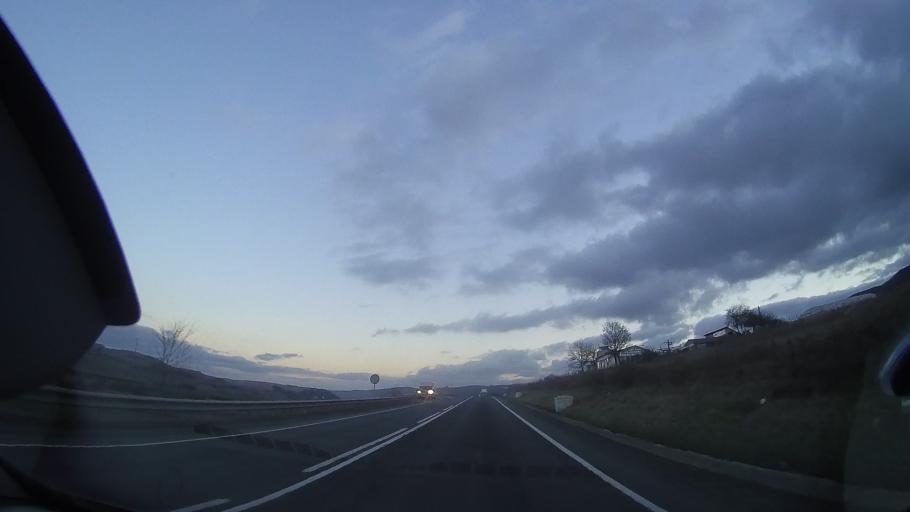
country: RO
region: Cluj
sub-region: Comuna Capusu Mare
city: Capusu Mare
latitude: 46.8045
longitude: 23.2607
